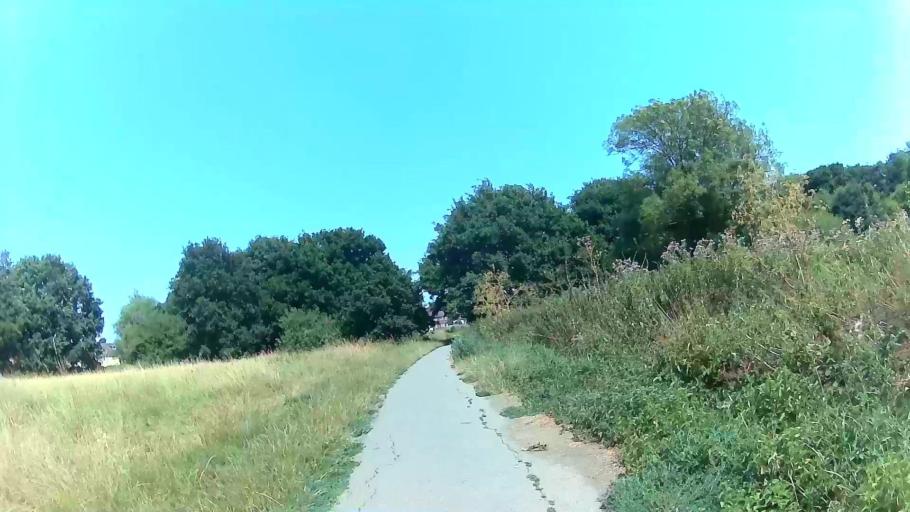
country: GB
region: England
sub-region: Greater London
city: Hornchurch
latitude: 51.5468
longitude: 0.2232
